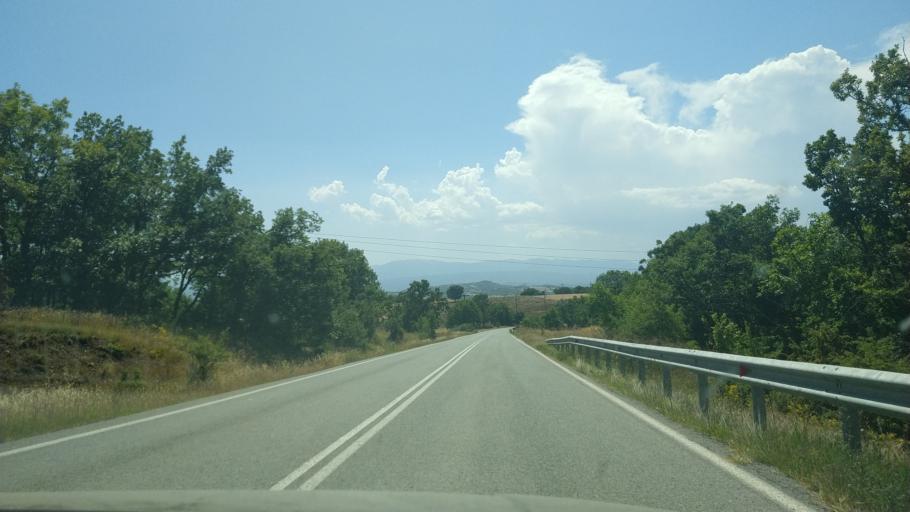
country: GR
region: West Macedonia
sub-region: Nomos Grevenon
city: Grevena
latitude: 39.9795
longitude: 21.5118
